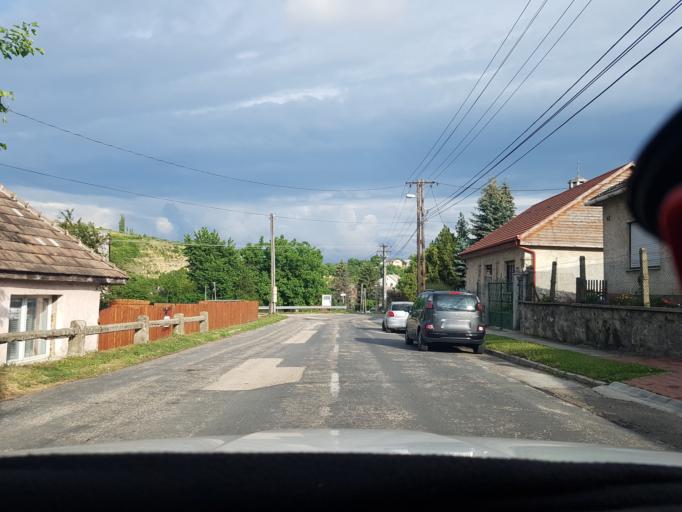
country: HU
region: Komarom-Esztergom
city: Labatlan
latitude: 47.7453
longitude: 18.5007
